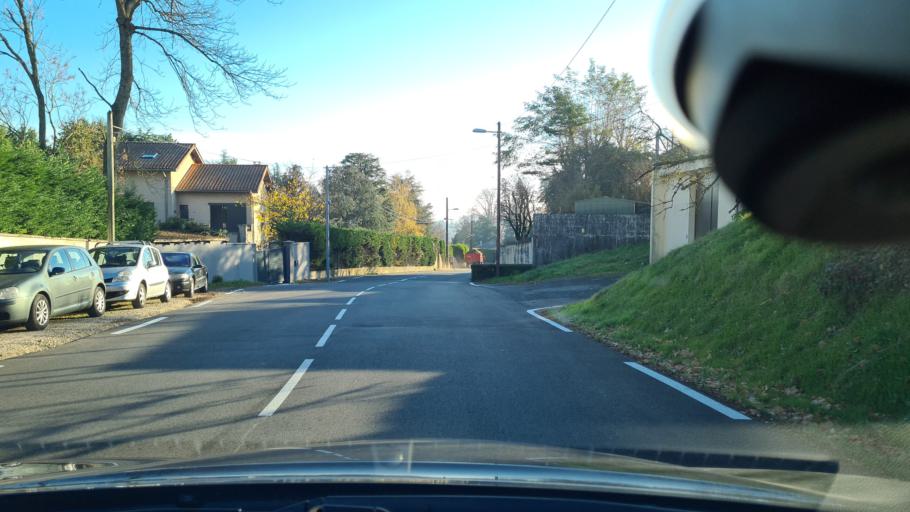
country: FR
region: Rhone-Alpes
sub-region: Departement du Rhone
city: Fontaines-sur-Saone
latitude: 45.8256
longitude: 4.8099
